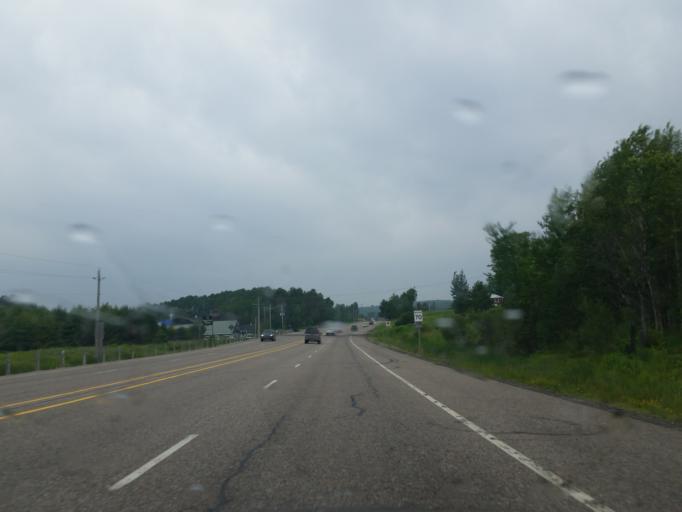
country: CA
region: Ontario
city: Huntsville
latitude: 45.3409
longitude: -79.1826
